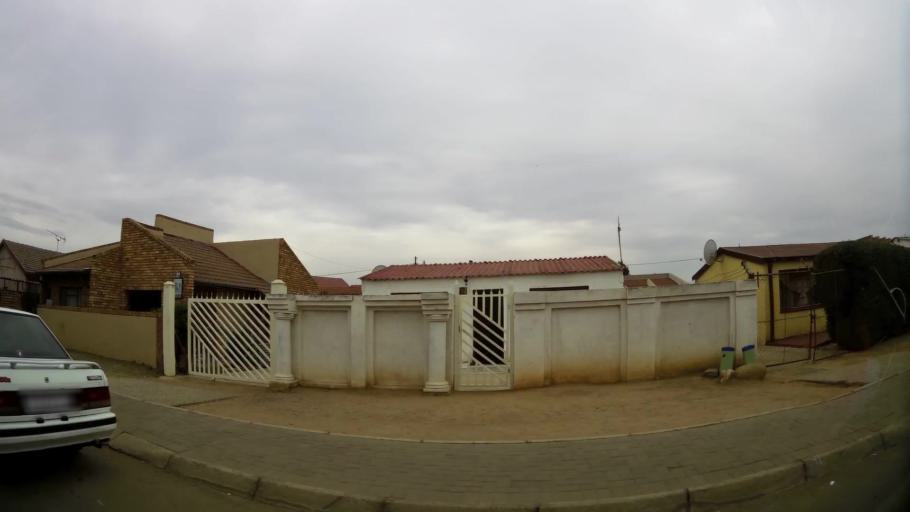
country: ZA
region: Gauteng
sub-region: City of Tshwane Metropolitan Municipality
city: Pretoria
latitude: -25.7112
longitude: 28.3417
